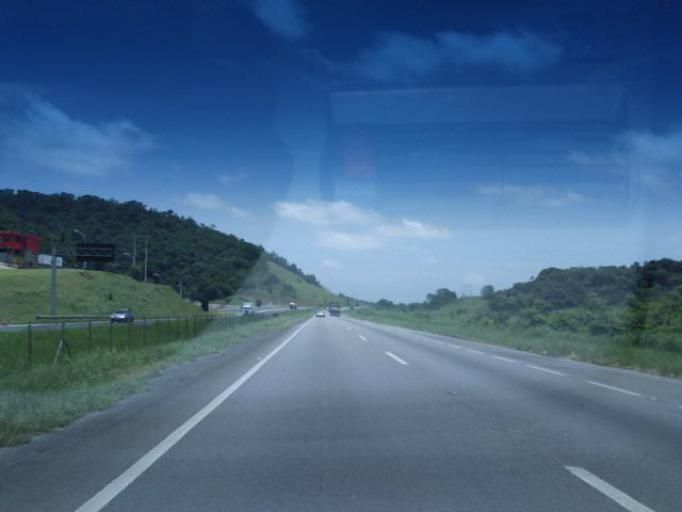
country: BR
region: Sao Paulo
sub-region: Miracatu
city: Miracatu
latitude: -24.2902
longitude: -47.4648
